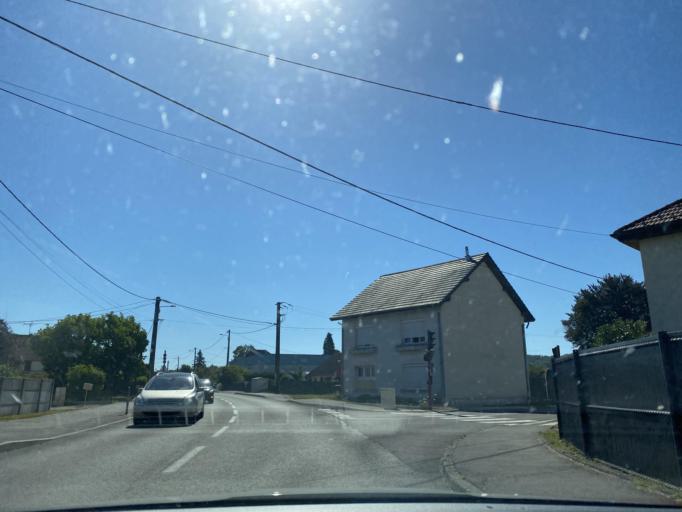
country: FR
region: Franche-Comte
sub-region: Departement de la Haute-Saone
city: Champagney
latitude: 47.7033
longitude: 6.6929
